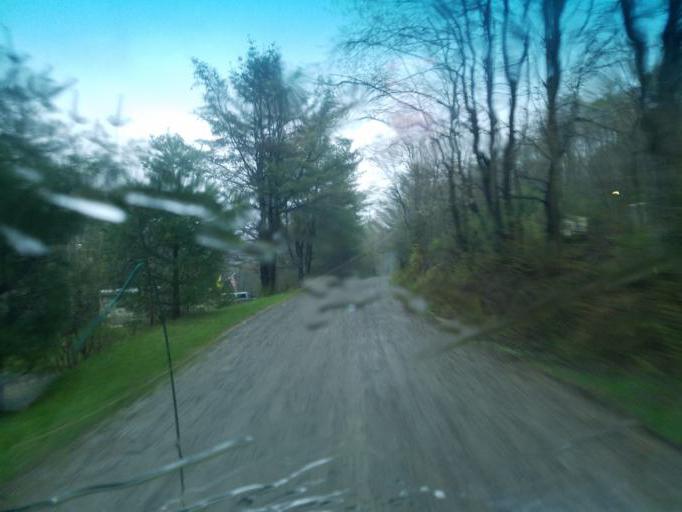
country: US
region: Pennsylvania
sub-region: Tioga County
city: Westfield
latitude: 41.8947
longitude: -77.7080
